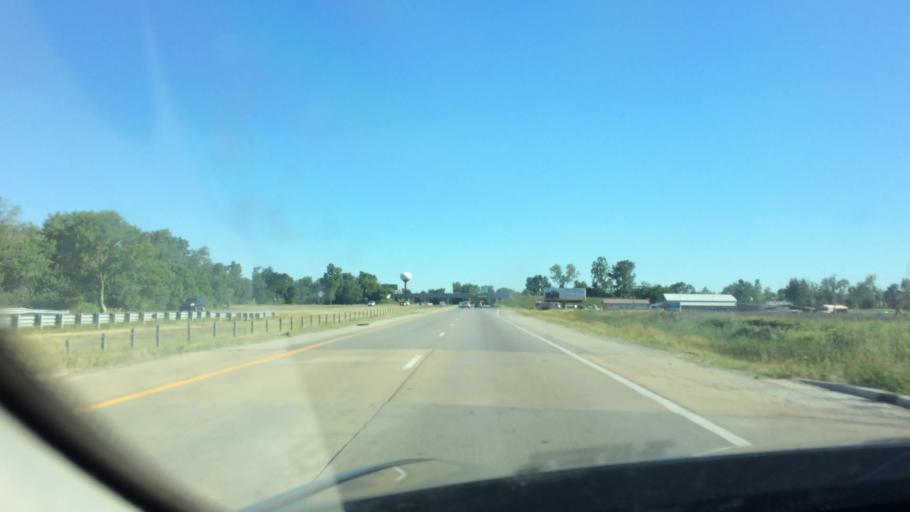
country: US
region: Michigan
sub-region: Washtenaw County
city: Milan
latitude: 42.0750
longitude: -83.6705
